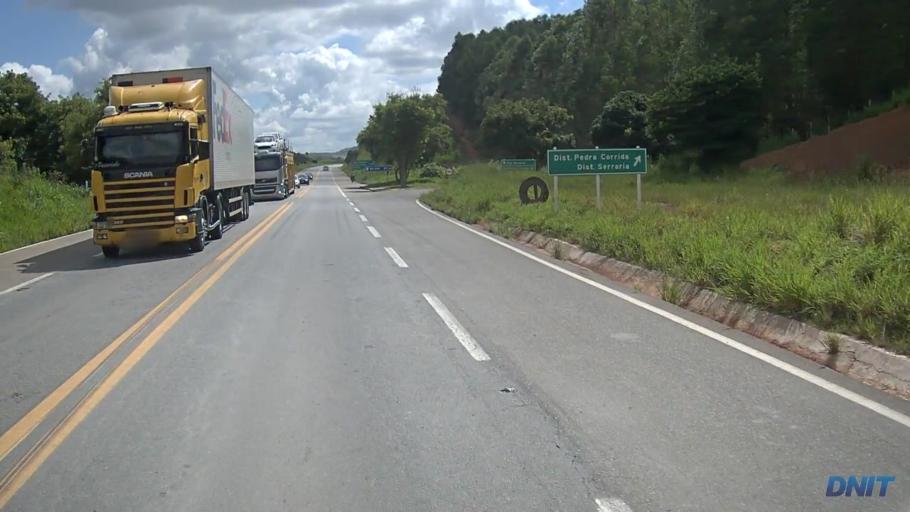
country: BR
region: Minas Gerais
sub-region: Governador Valadares
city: Governador Valadares
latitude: -19.0708
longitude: -42.1757
